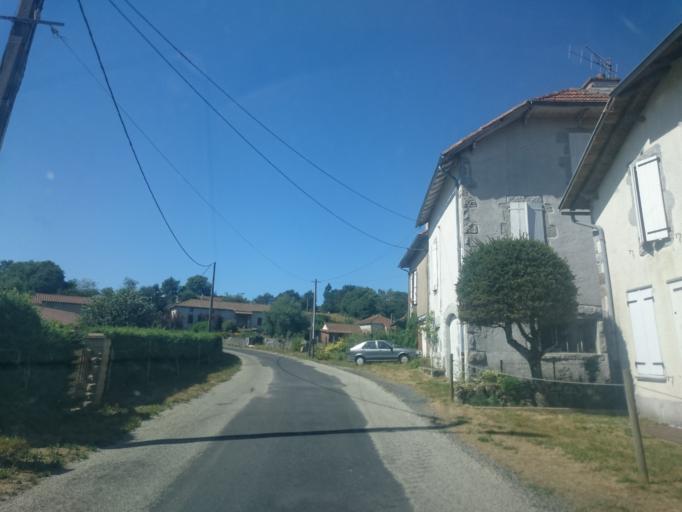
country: FR
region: Auvergne
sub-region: Departement du Cantal
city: Laroquebrou
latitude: 44.8998
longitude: 2.1782
